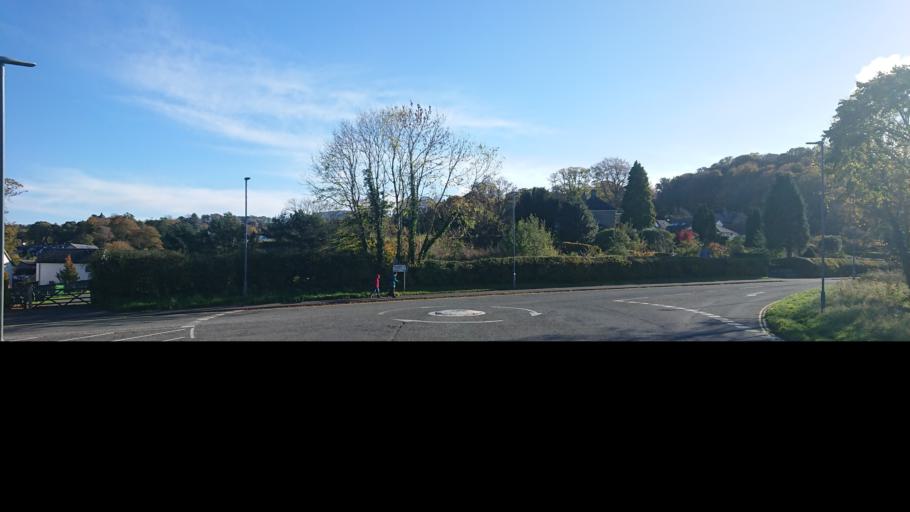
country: GB
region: England
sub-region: Cumbria
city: Keswick
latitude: 54.5968
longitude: -3.1361
